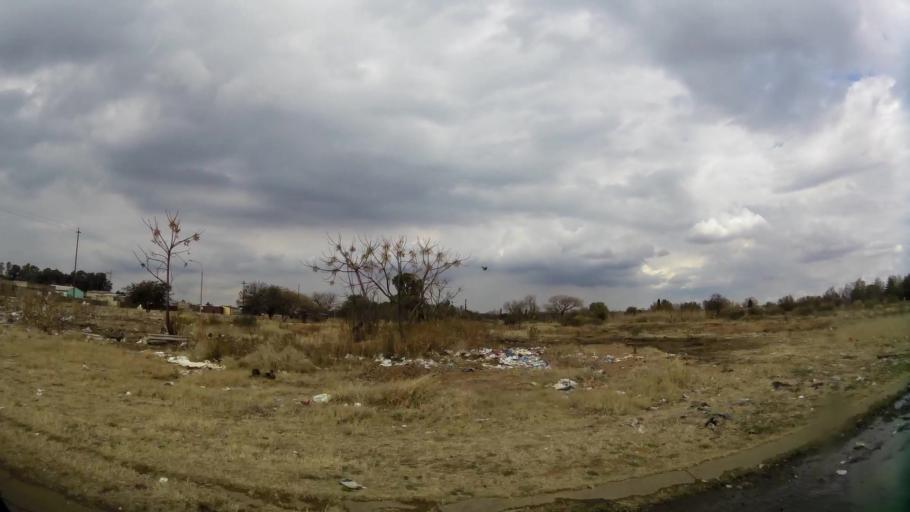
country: ZA
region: Gauteng
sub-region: Sedibeng District Municipality
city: Vanderbijlpark
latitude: -26.7035
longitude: 27.8052
